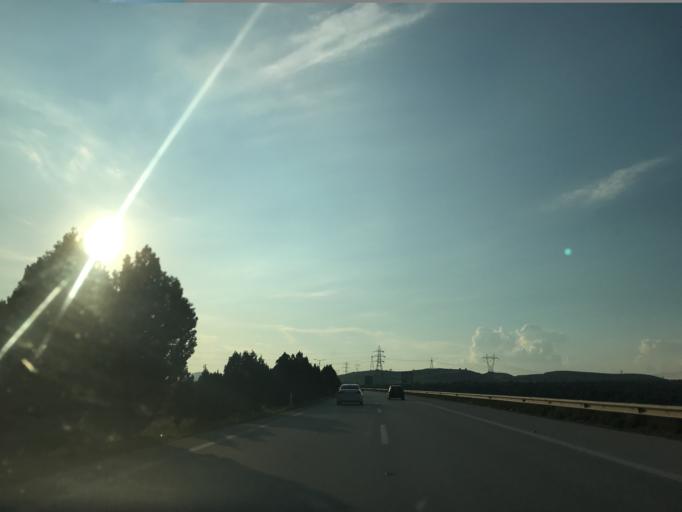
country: TR
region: Osmaniye
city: Toprakkale
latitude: 36.9729
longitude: 36.0704
